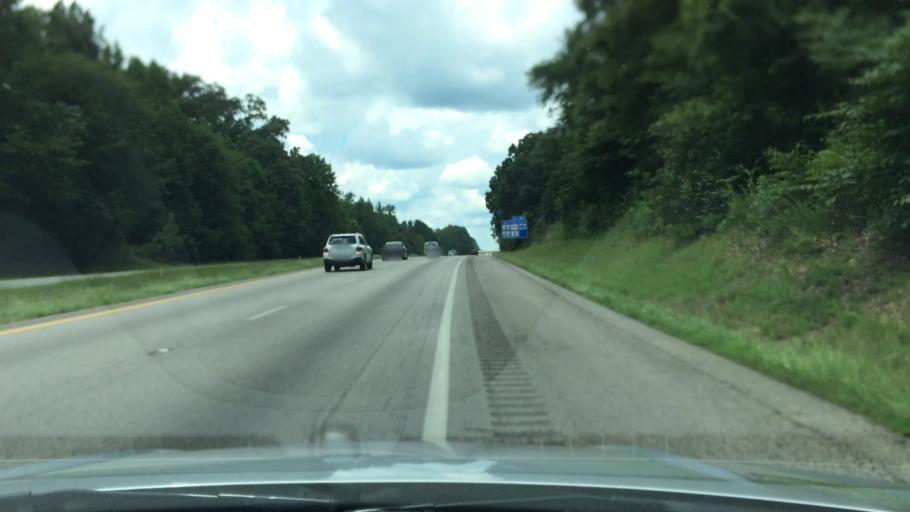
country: US
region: South Carolina
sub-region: Laurens County
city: Clinton
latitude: 34.4880
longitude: -81.8339
